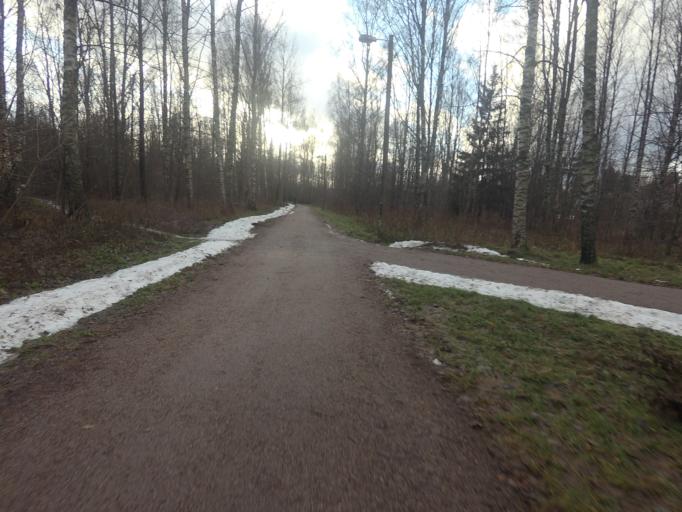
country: FI
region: Uusimaa
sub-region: Helsinki
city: Kilo
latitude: 60.1875
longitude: 24.7659
